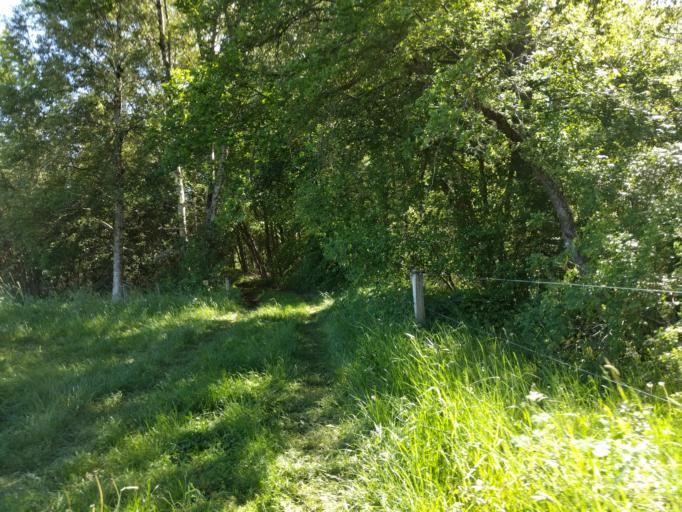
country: DK
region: South Denmark
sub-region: Kerteminde Kommune
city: Langeskov
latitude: 55.3843
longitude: 10.5904
